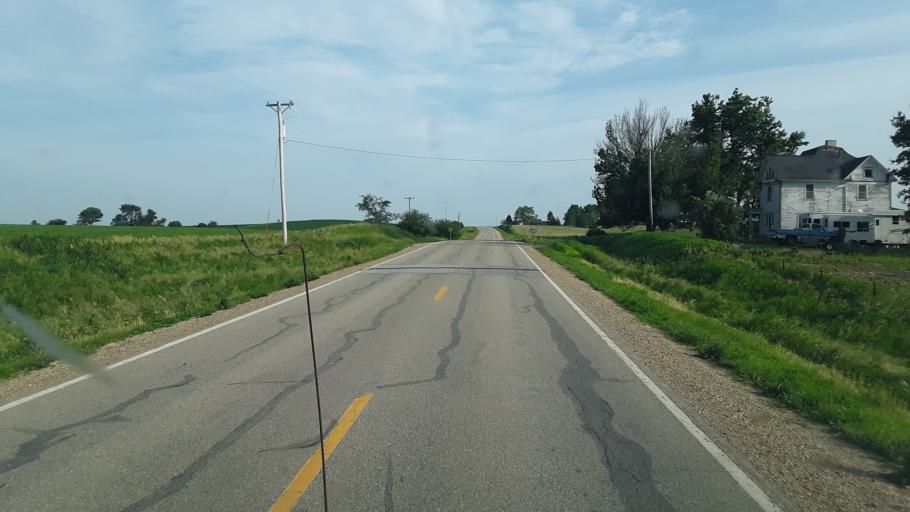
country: US
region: Iowa
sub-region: Tama County
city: Tama
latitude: 41.9670
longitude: -92.7085
